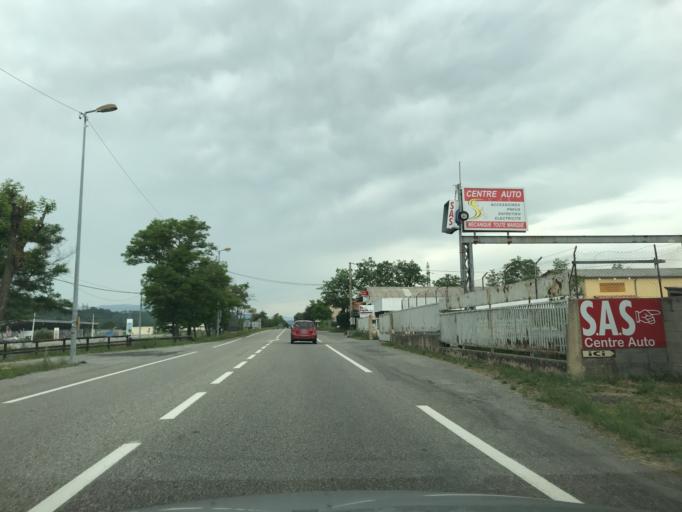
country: FR
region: Provence-Alpes-Cote d'Azur
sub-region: Departement des Alpes-de-Haute-Provence
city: Sisteron
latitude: 44.2095
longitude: 5.9299
